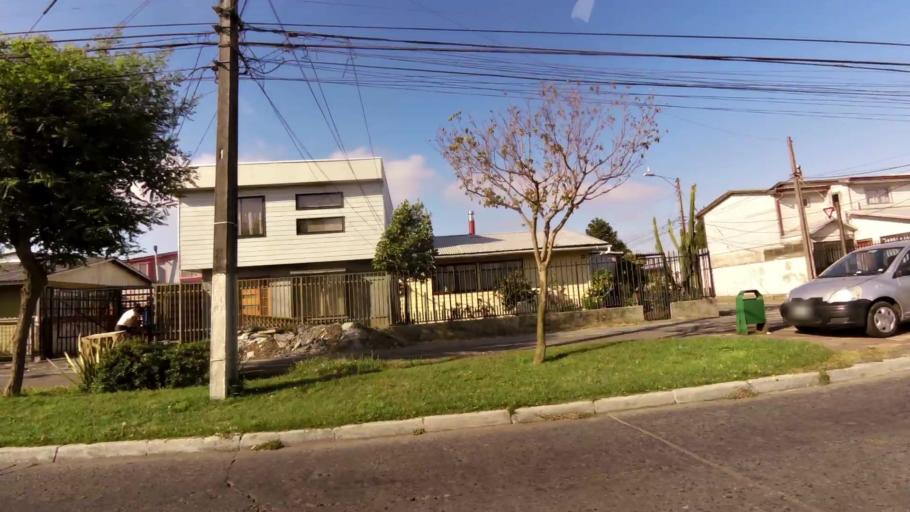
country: CL
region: Biobio
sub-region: Provincia de Concepcion
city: Concepcion
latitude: -36.7919
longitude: -73.1065
